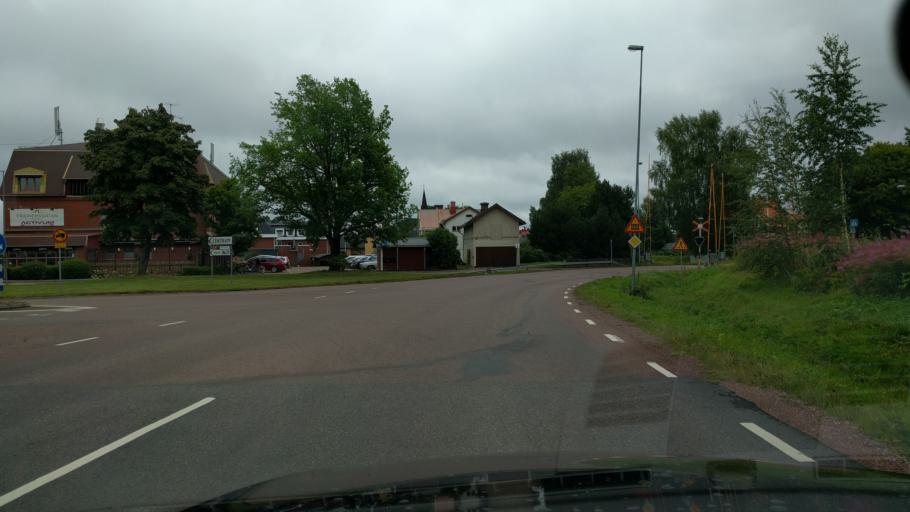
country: SE
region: Dalarna
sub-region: Mora Kommun
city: Mora
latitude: 61.0022
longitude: 14.5332
